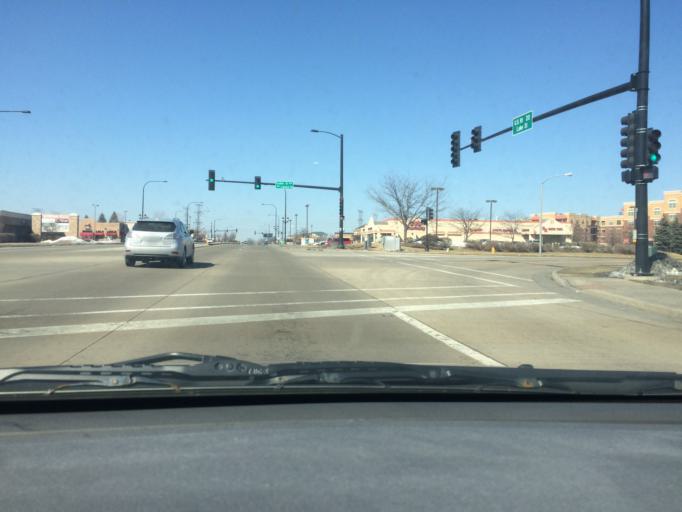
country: US
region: Illinois
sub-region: DuPage County
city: Itasca
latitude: 41.9463
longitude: -88.0216
